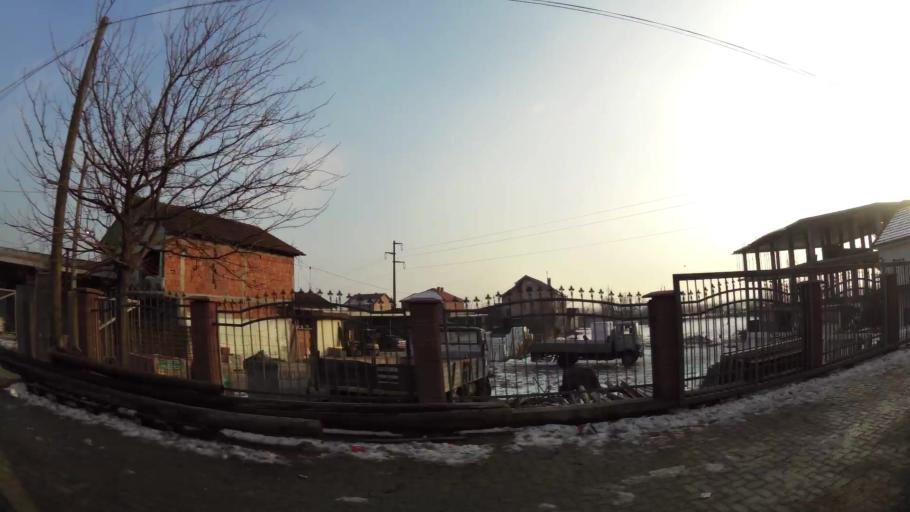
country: MK
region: Aracinovo
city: Arachinovo
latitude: 42.0239
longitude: 21.5529
